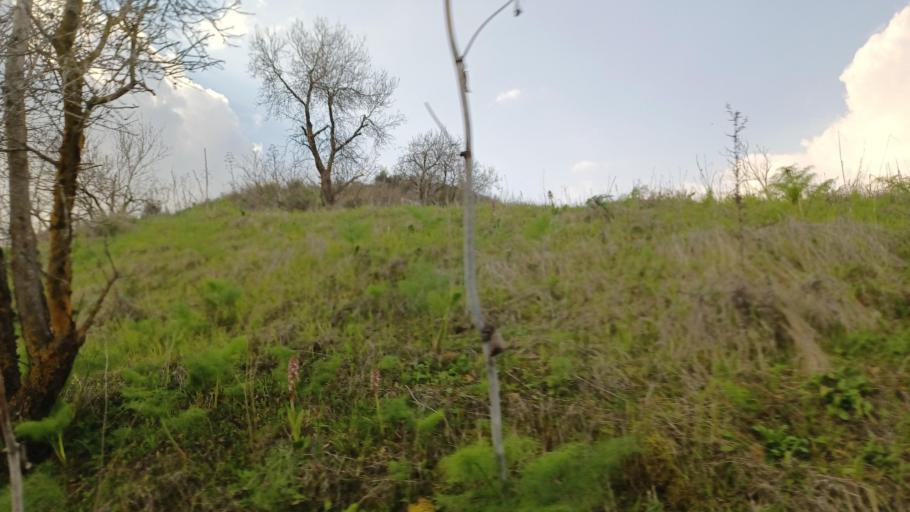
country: CY
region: Pafos
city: Polis
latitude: 35.0029
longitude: 32.5078
